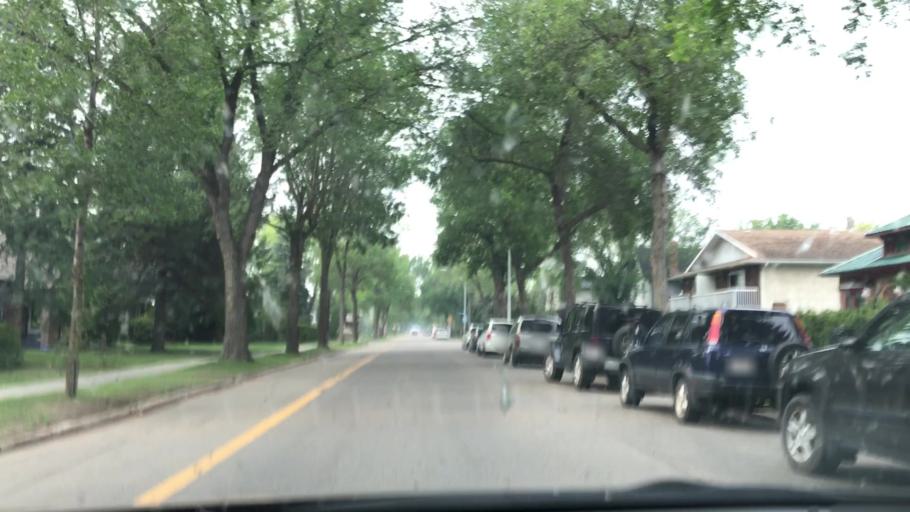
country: CA
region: Alberta
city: Edmonton
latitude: 53.5612
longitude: -113.5412
